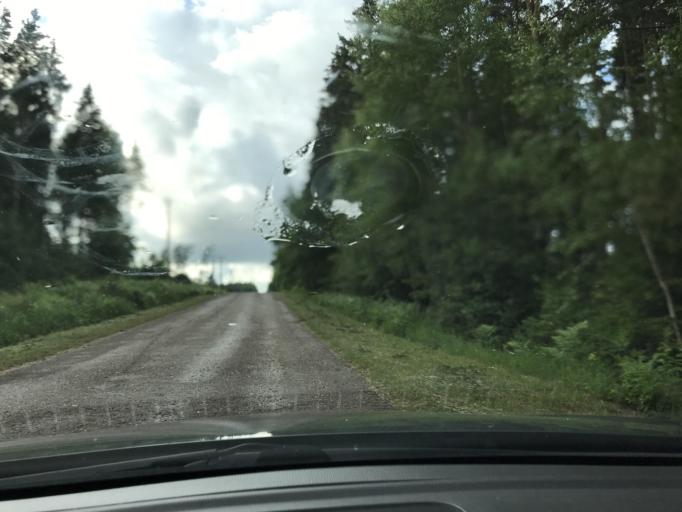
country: LV
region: Alsunga
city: Alsunga
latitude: 56.9871
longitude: 21.6296
